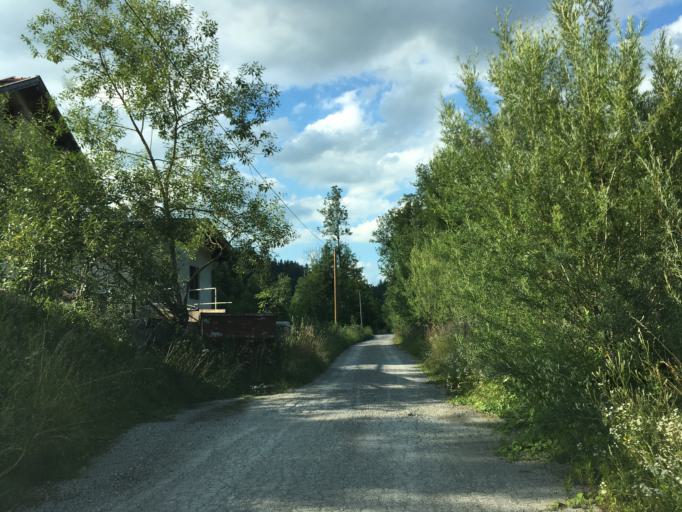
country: DE
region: Bavaria
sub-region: Upper Bavaria
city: Miesbach
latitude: 47.7881
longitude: 11.7873
